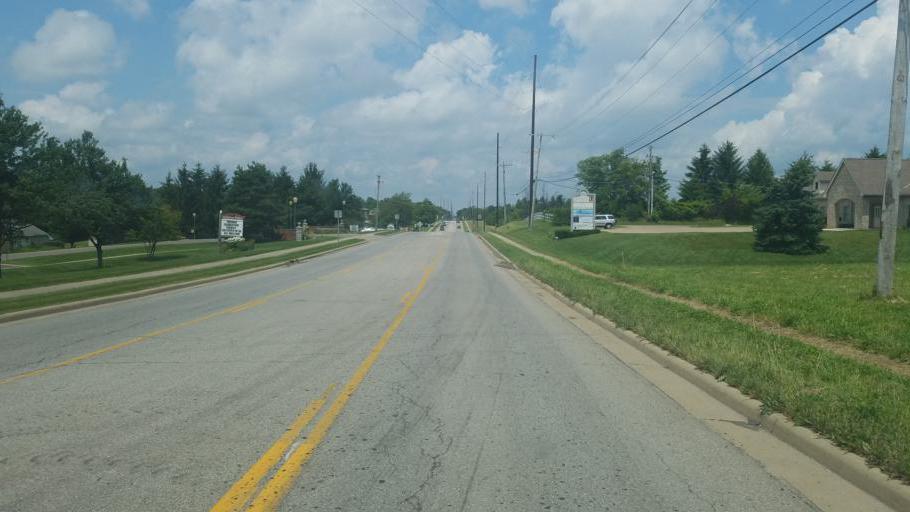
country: US
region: Ohio
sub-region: Richland County
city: Mansfield
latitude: 40.7412
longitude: -82.5517
